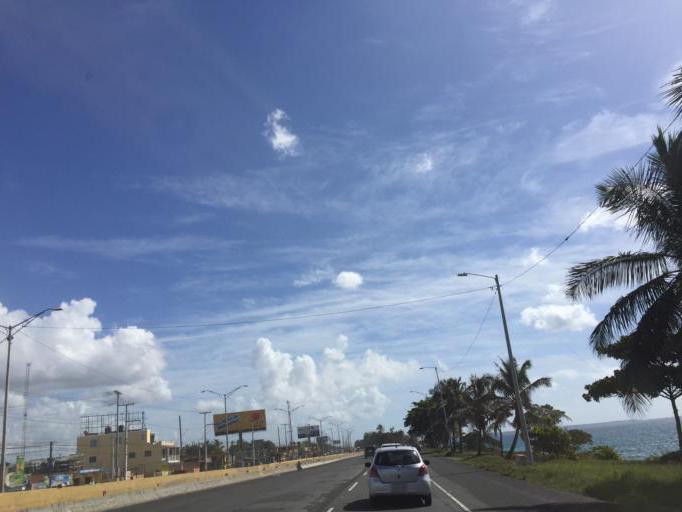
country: DO
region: Santo Domingo
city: Guerra
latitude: 18.4626
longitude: -69.7376
